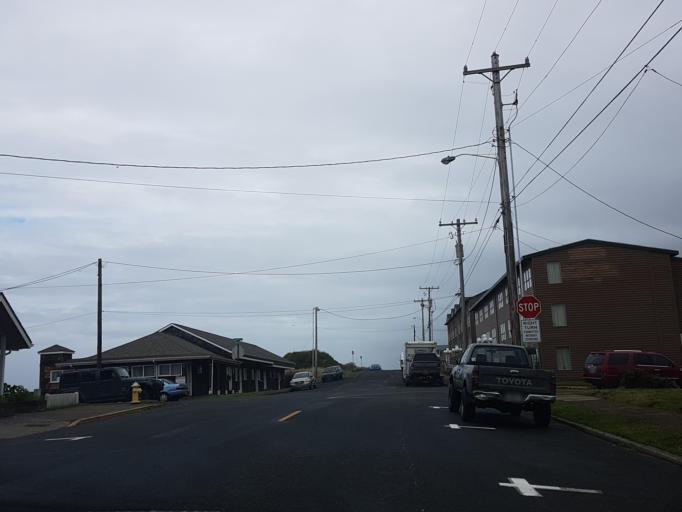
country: US
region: Oregon
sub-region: Lincoln County
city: Newport
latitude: 44.6416
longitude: -124.0607
